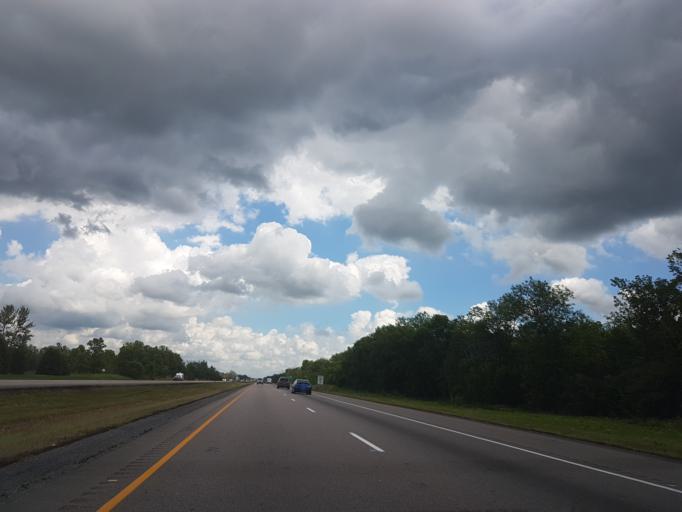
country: CA
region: Ontario
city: Deseronto
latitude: 44.2347
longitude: -77.1341
